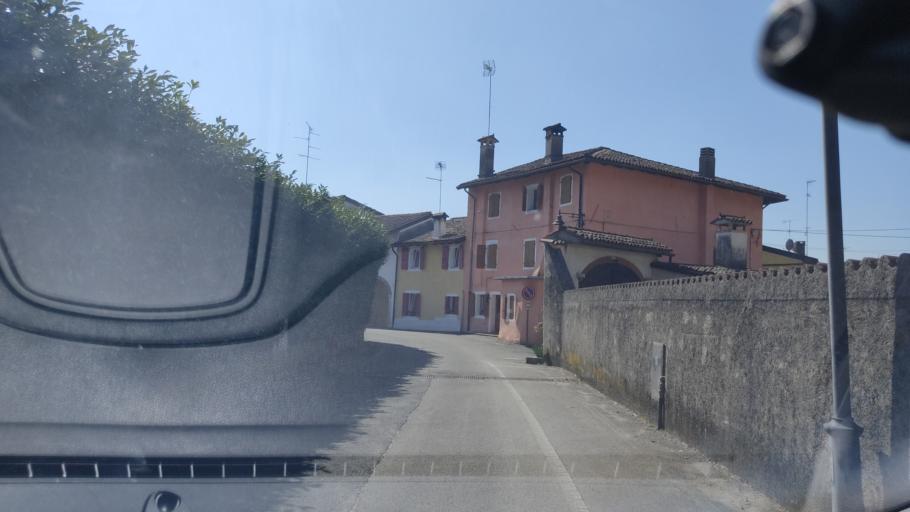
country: IT
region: Friuli Venezia Giulia
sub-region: Provincia di Pordenone
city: Budoia
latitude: 46.0358
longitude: 12.5276
